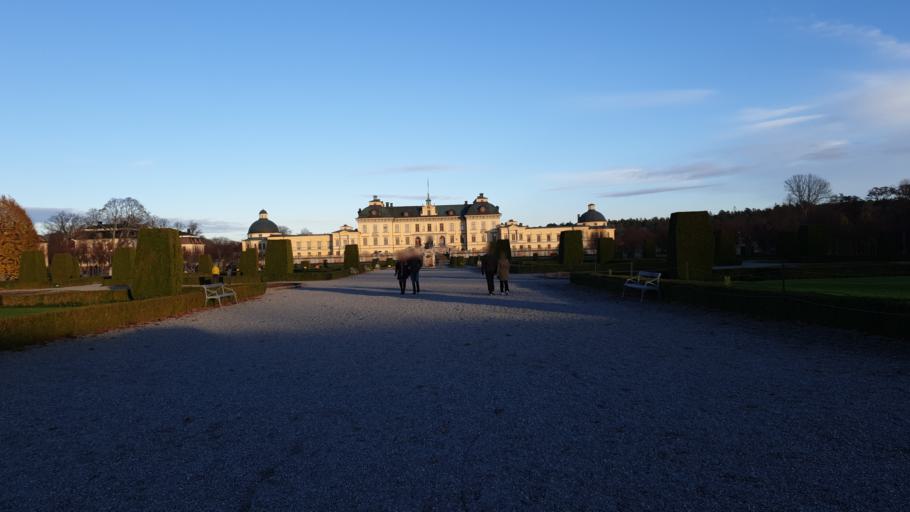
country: SE
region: Stockholm
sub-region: Stockholms Kommun
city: Bromma
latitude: 59.3207
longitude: 17.8818
